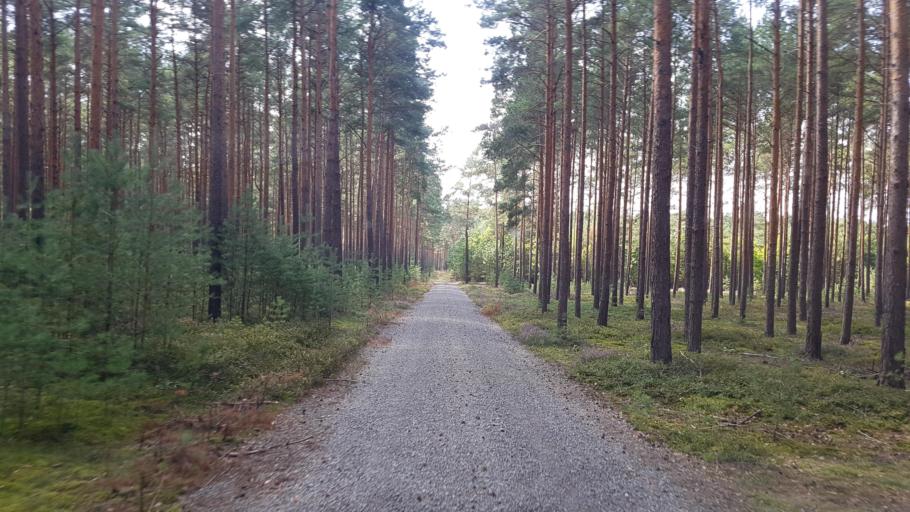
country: DE
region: Brandenburg
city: Hohenbucko
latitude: 51.7612
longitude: 13.5422
